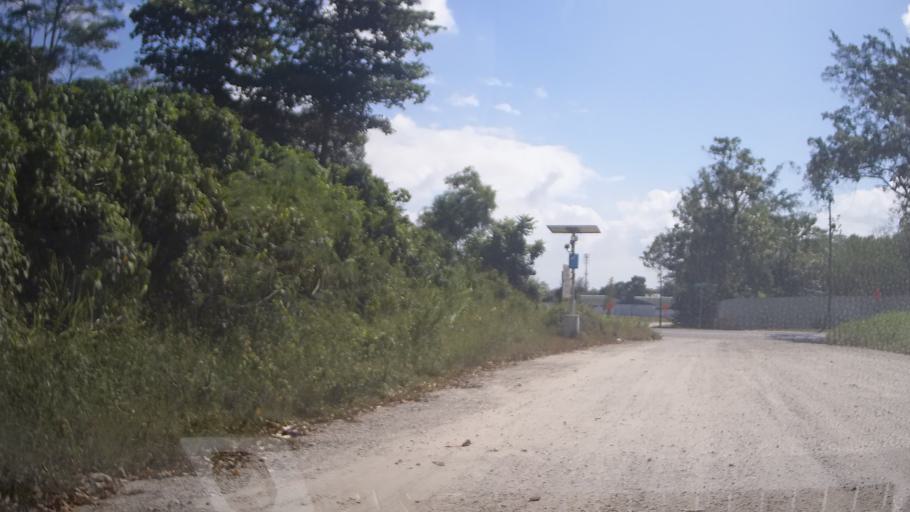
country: MY
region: Johor
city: Johor Bahru
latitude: 1.4346
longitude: 103.7077
